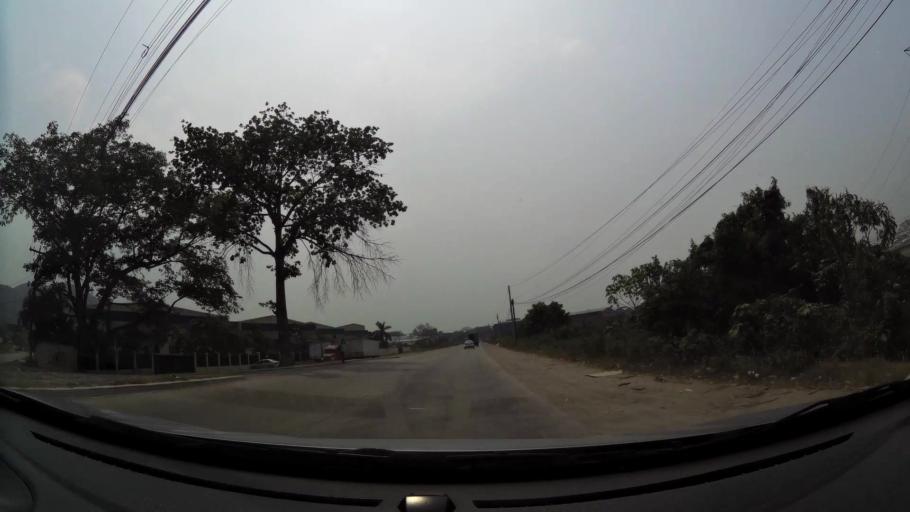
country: HN
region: Cortes
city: Chotepe
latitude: 15.4630
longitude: -87.9667
